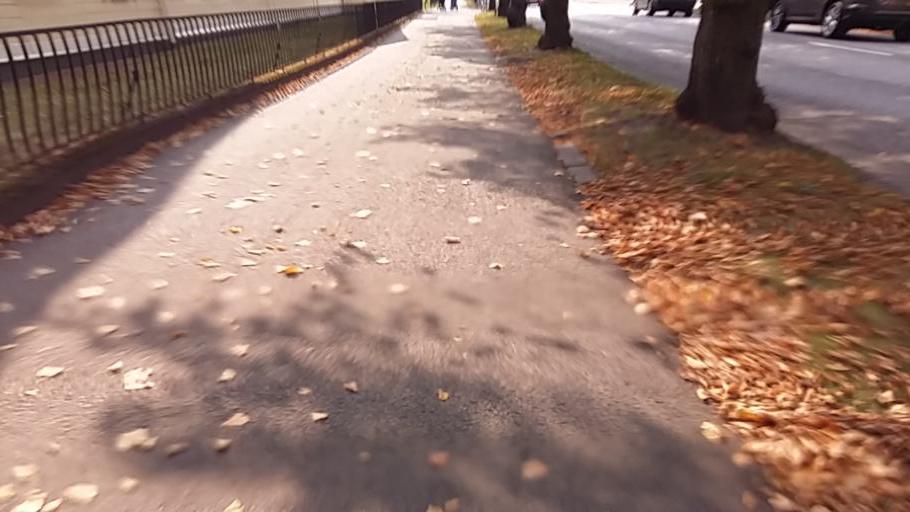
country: SE
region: Joenkoeping
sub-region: Jonkopings Kommun
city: Jonkoping
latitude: 57.7752
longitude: 14.1584
